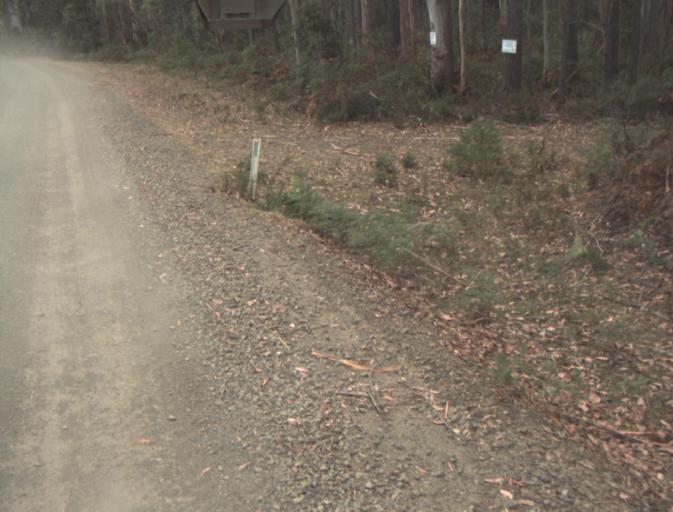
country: AU
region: Tasmania
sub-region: Dorset
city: Scottsdale
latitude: -41.4252
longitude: 147.5139
